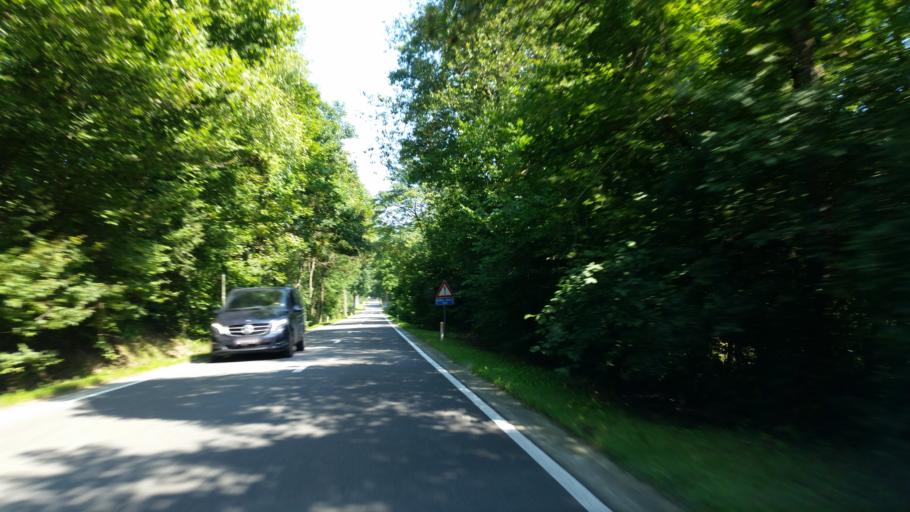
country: BE
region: Wallonia
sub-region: Province du Luxembourg
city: Marche-en-Famenne
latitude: 50.2924
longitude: 5.2844
